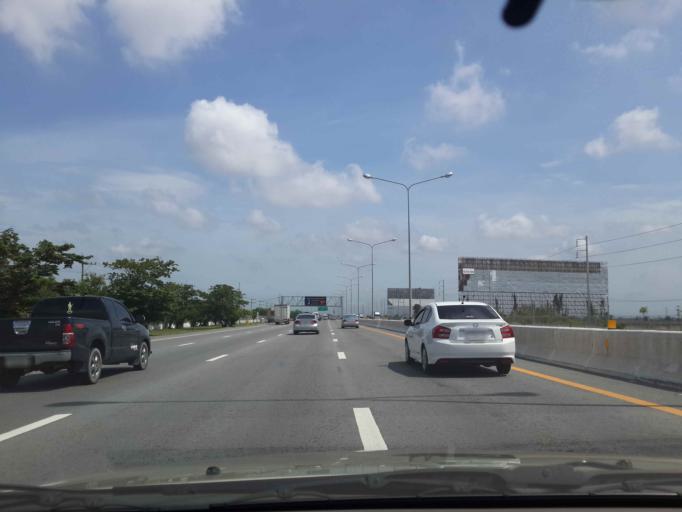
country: TH
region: Chachoengsao
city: Bang Pakong
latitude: 13.5865
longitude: 100.9689
